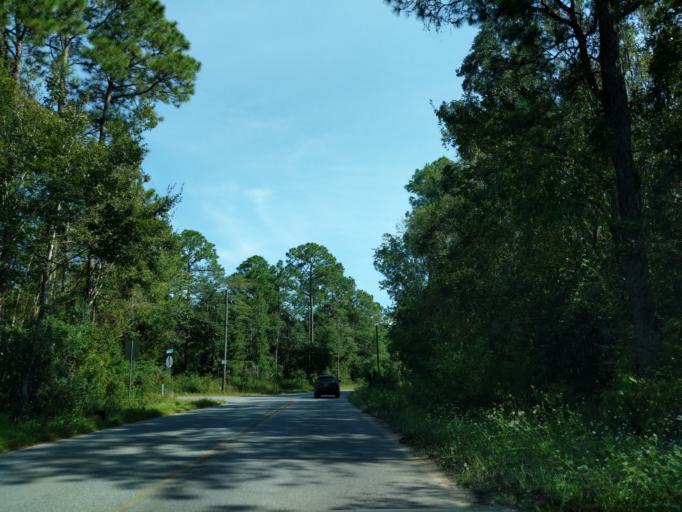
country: US
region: Florida
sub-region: Okaloosa County
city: Crestview
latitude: 30.7033
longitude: -86.5809
